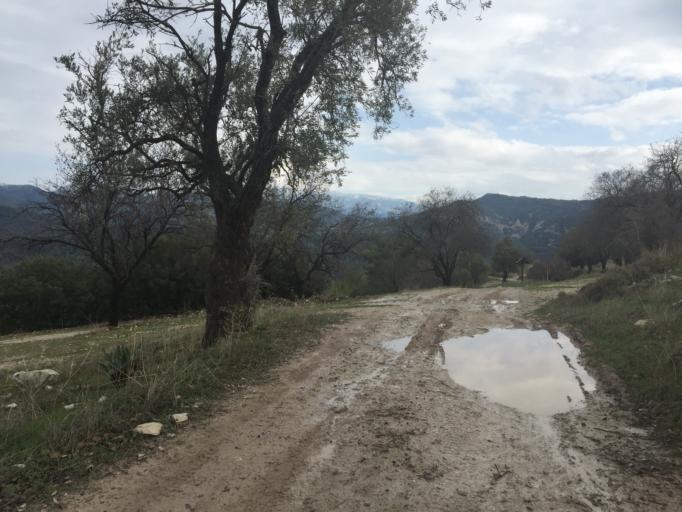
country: CY
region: Limassol
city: Pachna
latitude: 34.8897
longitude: 32.6618
